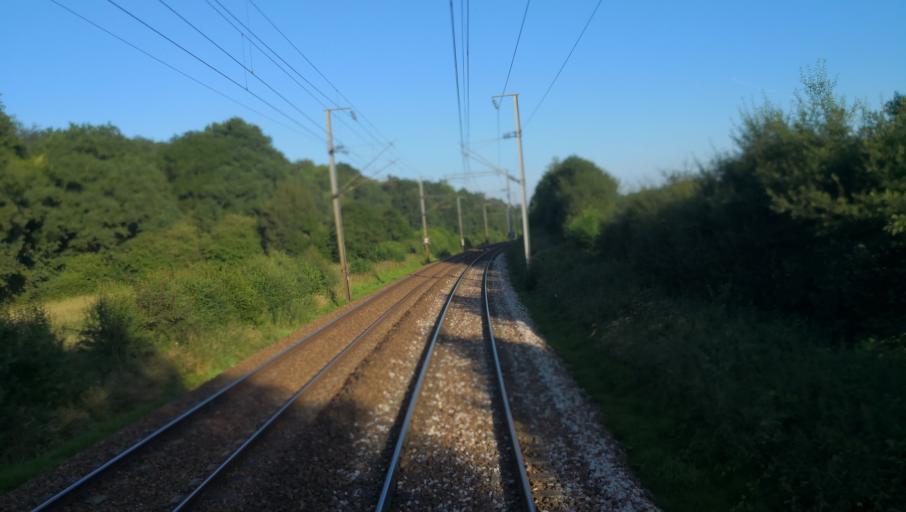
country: FR
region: Haute-Normandie
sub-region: Departement de l'Eure
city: Bernay
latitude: 49.0918
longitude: 0.5610
